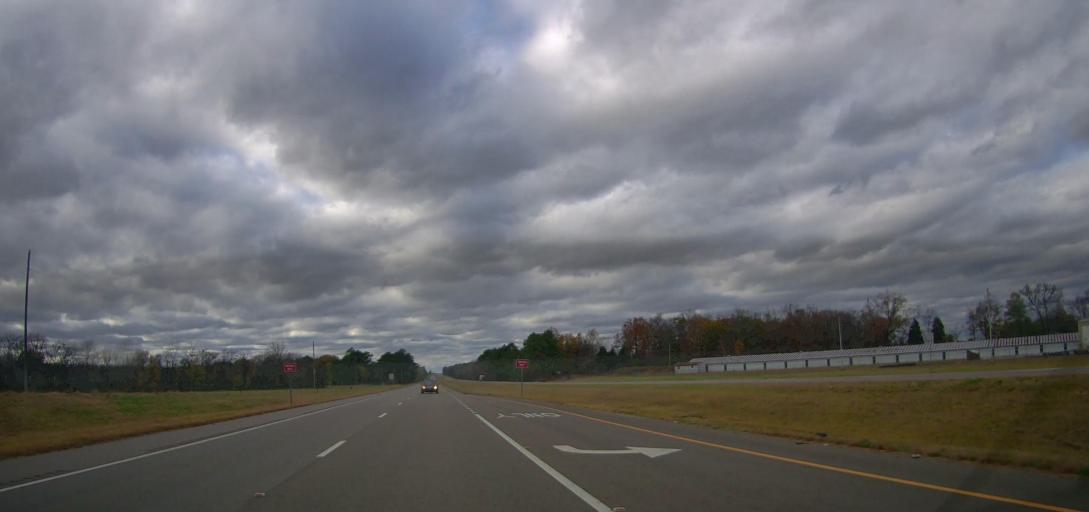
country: US
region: Alabama
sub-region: Morgan County
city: Danville
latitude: 34.3449
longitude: -87.0339
